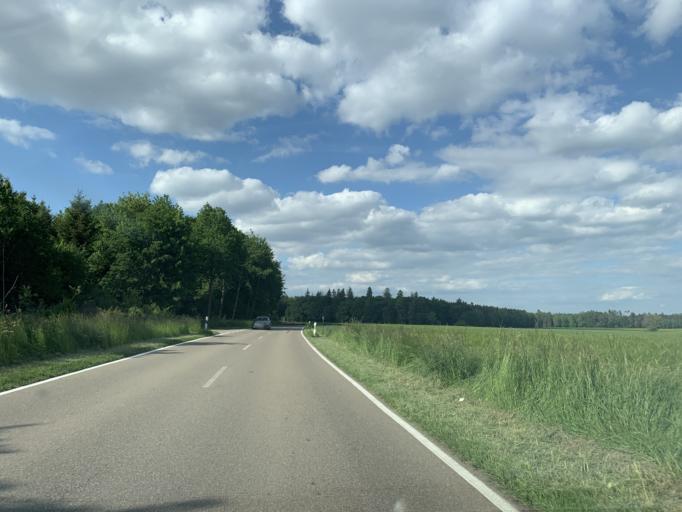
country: DE
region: Baden-Wuerttemberg
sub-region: Tuebingen Region
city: Huttisheim
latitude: 48.3118
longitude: 9.9394
